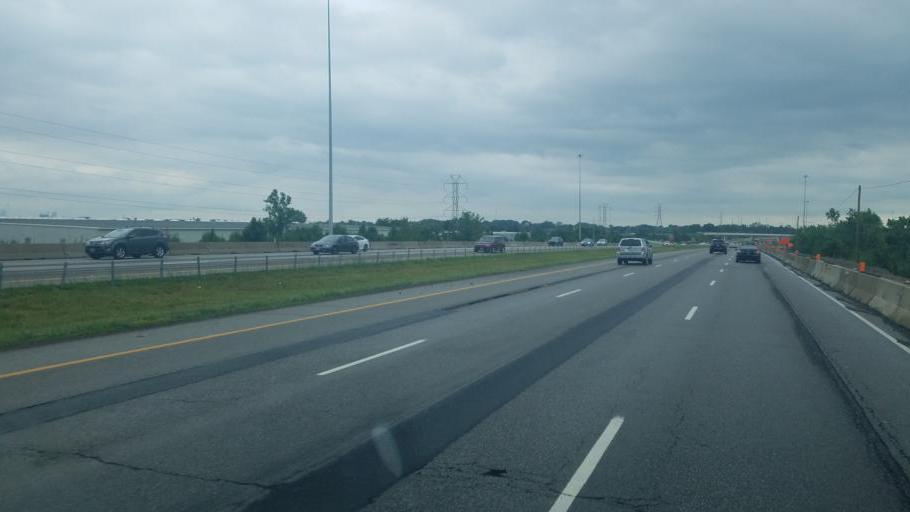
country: US
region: Ohio
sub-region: Franklin County
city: Hilliard
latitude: 40.0095
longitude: -83.1194
